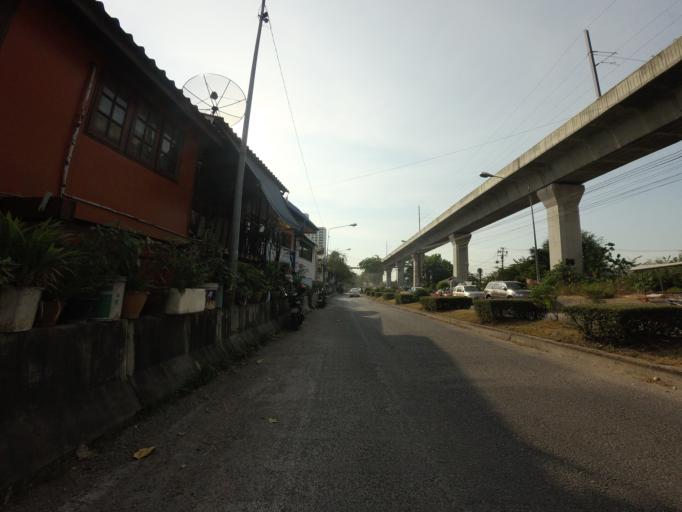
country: TH
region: Bangkok
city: Watthana
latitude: 13.7430
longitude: 100.5978
